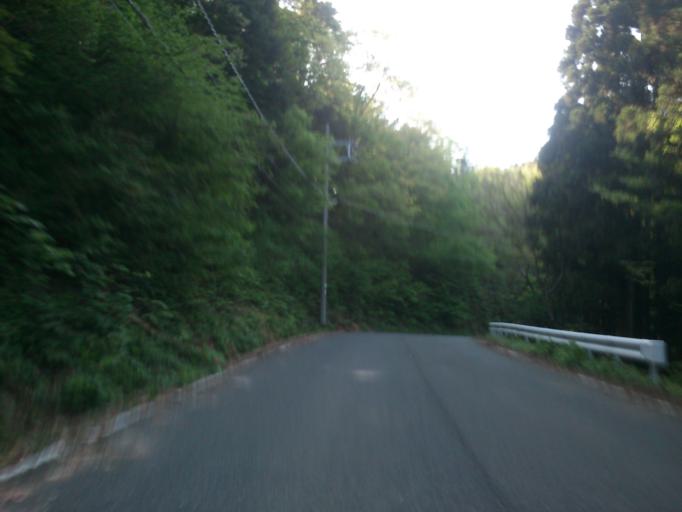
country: JP
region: Kyoto
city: Miyazu
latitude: 35.7125
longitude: 135.1942
